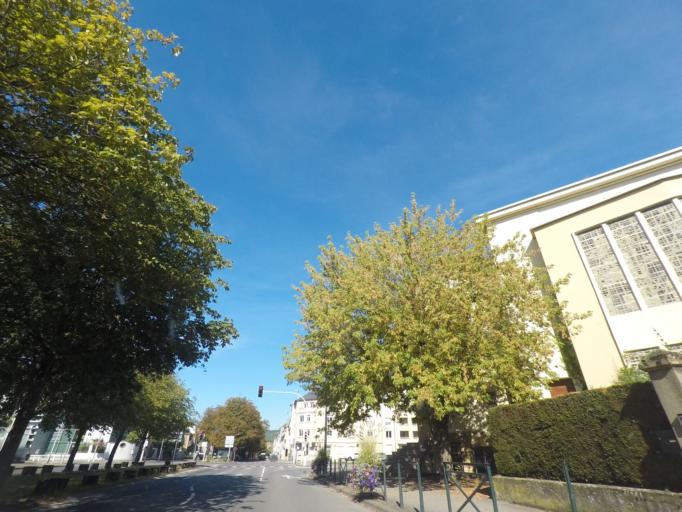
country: FR
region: Lorraine
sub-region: Departement de la Moselle
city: Thionville
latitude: 49.3612
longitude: 6.1662
